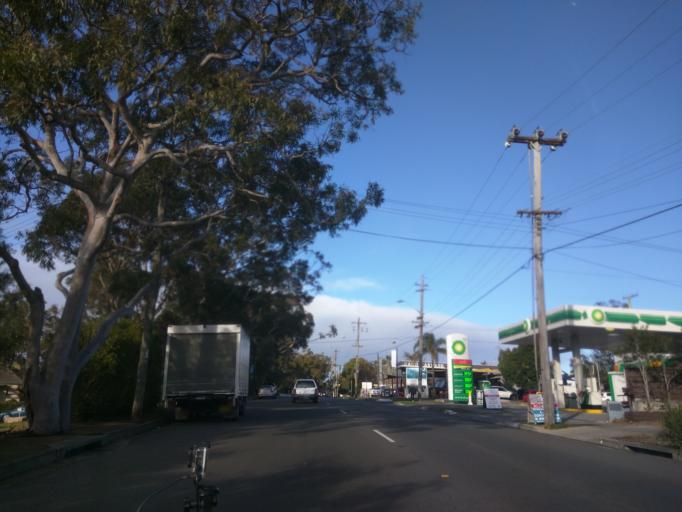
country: AU
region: New South Wales
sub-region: Hurstville
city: Lugarno
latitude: -33.9772
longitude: 151.0473
